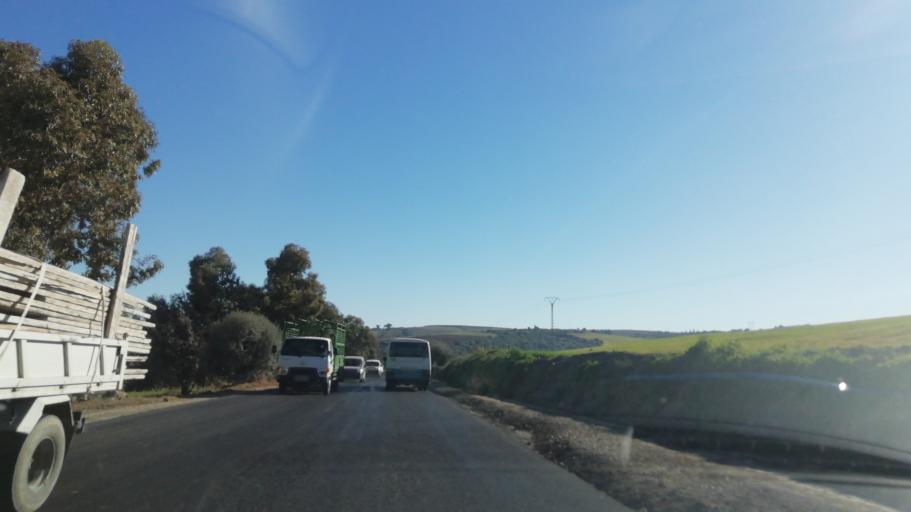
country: DZ
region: Relizane
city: Smala
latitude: 35.6715
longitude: 0.8050
